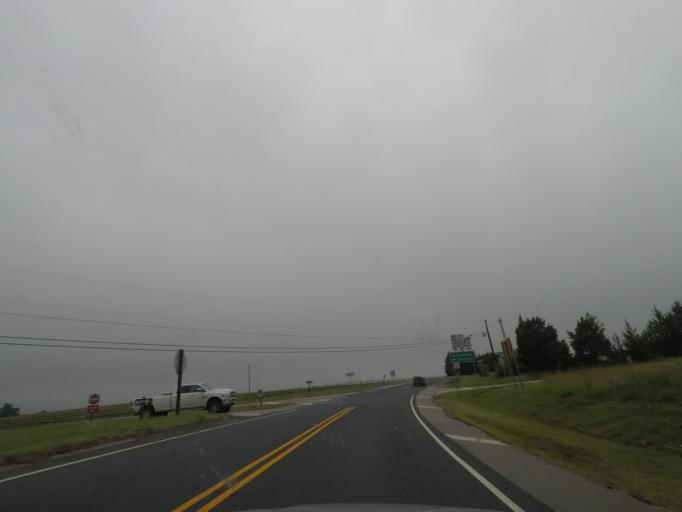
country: US
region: Virginia
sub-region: Charlotte County
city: Charlotte Court House
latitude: 37.0645
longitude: -78.4728
